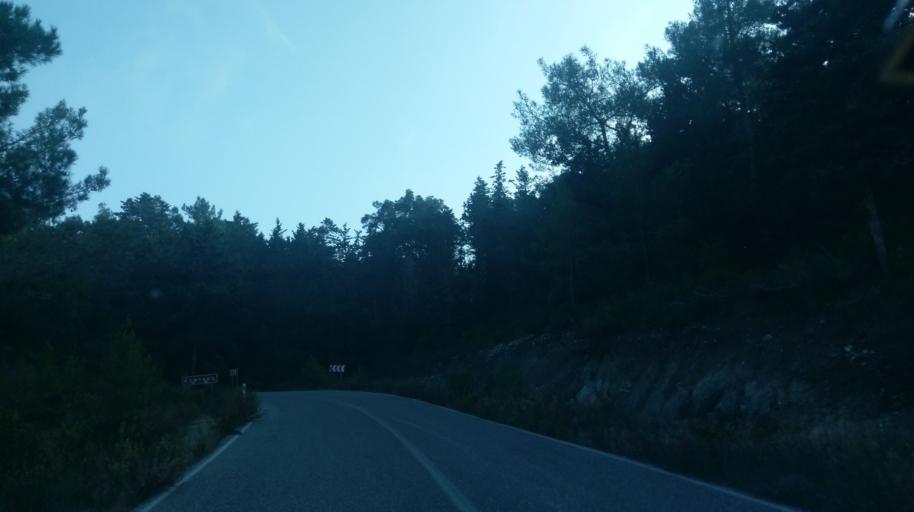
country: CY
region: Ammochostos
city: Trikomo
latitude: 35.3882
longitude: 33.8956
